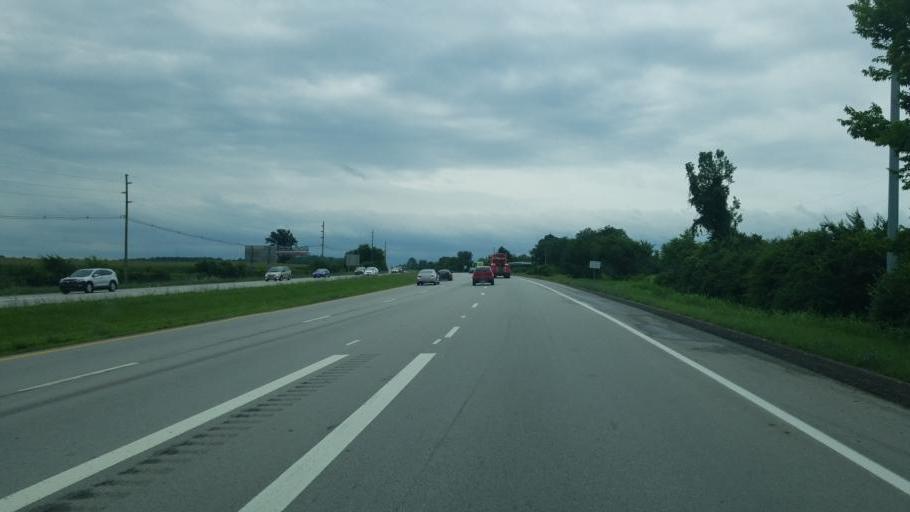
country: US
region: Ohio
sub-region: Franklin County
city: Obetz
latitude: 39.8709
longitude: -83.0054
